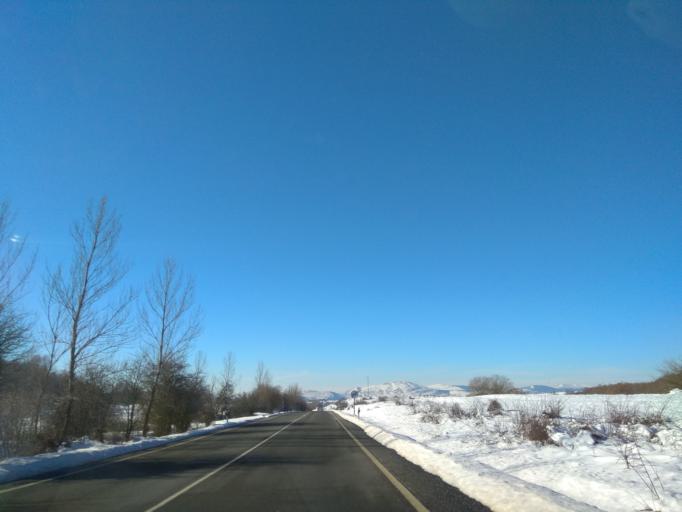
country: ES
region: Cantabria
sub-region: Provincia de Cantabria
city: San Martin de Elines
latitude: 42.9383
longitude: -3.7016
